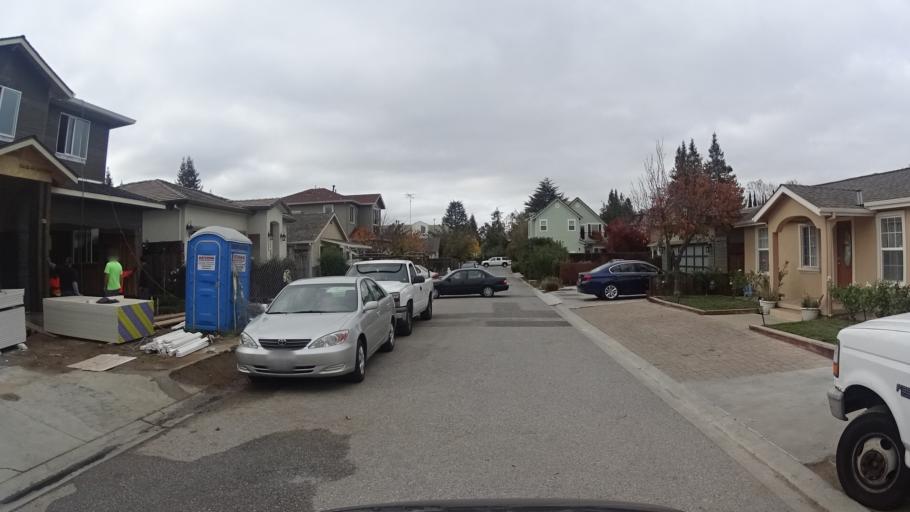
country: US
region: California
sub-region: Santa Clara County
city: Sunnyvale
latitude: 37.3536
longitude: -122.0404
